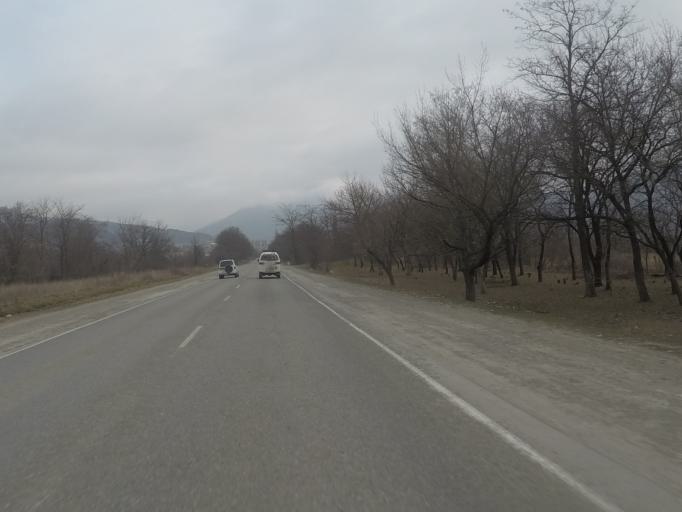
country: GE
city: Zhinvali
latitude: 42.0921
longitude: 44.7599
